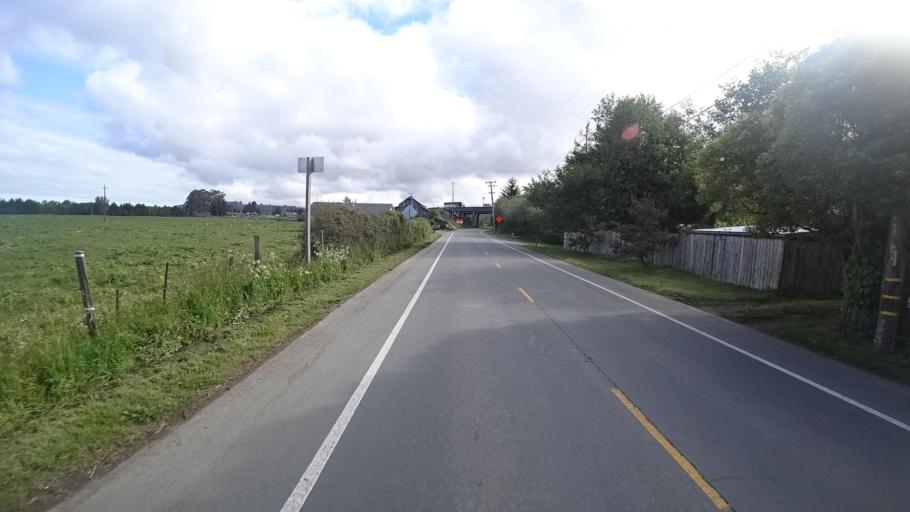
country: US
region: California
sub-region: Humboldt County
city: Arcata
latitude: 40.8904
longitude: -124.0818
